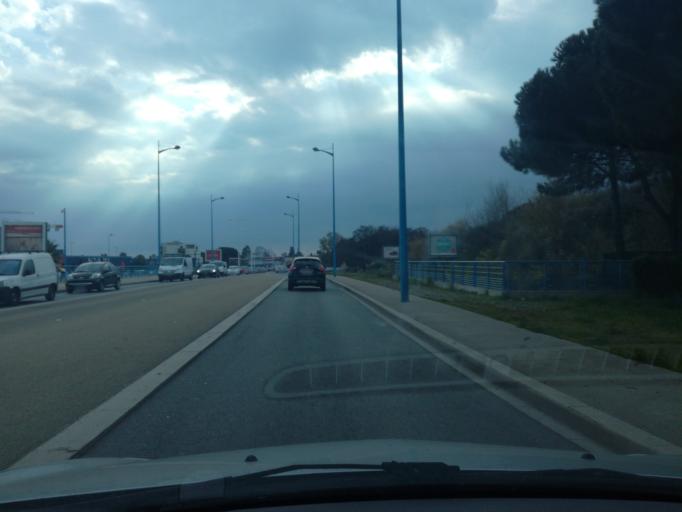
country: FR
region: Provence-Alpes-Cote d'Azur
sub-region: Departement des Alpes-Maritimes
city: Mandelieu-la-Napoule
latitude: 43.5538
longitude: 6.9546
